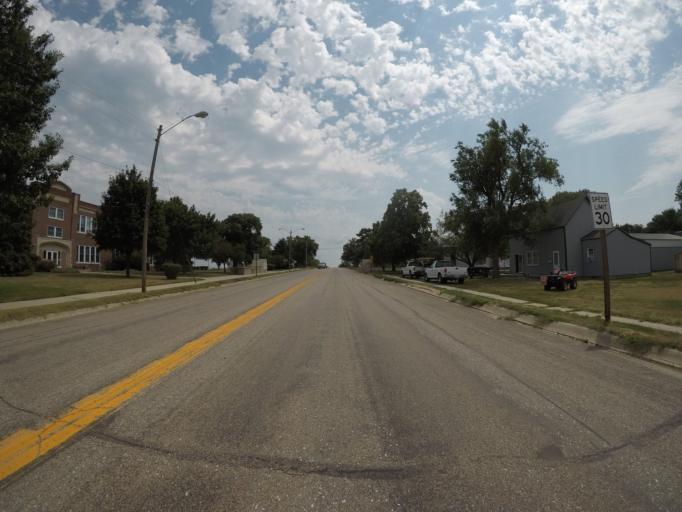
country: US
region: Nebraska
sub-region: Clay County
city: Clay Center
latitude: 40.5235
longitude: -98.0516
